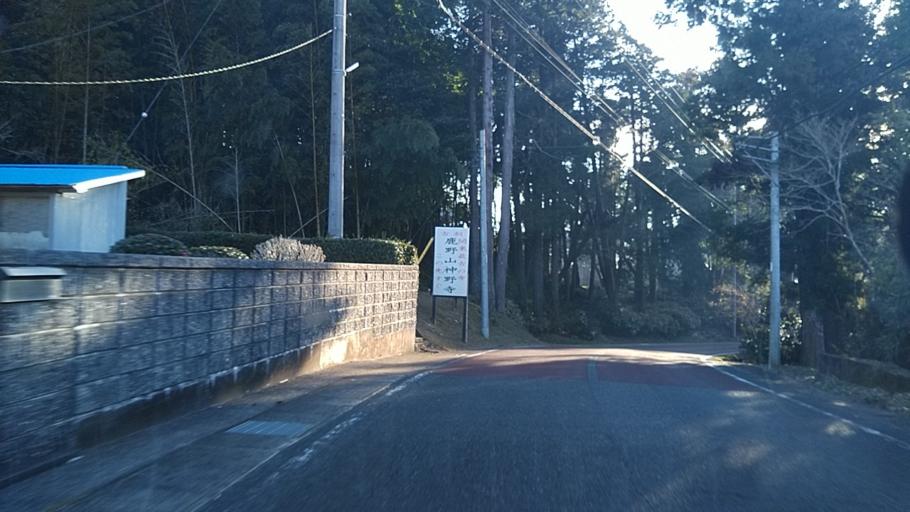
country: JP
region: Chiba
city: Kimitsu
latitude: 35.2548
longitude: 139.9619
